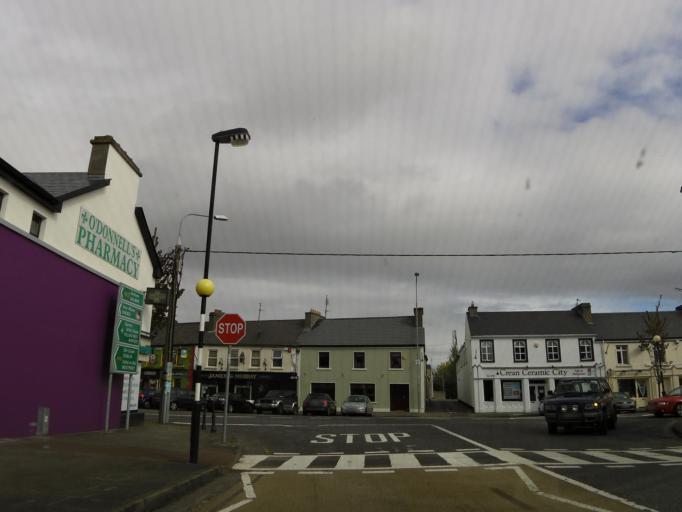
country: IE
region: Connaught
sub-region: Sligo
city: Tobercurry
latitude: 53.9637
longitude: -8.7942
